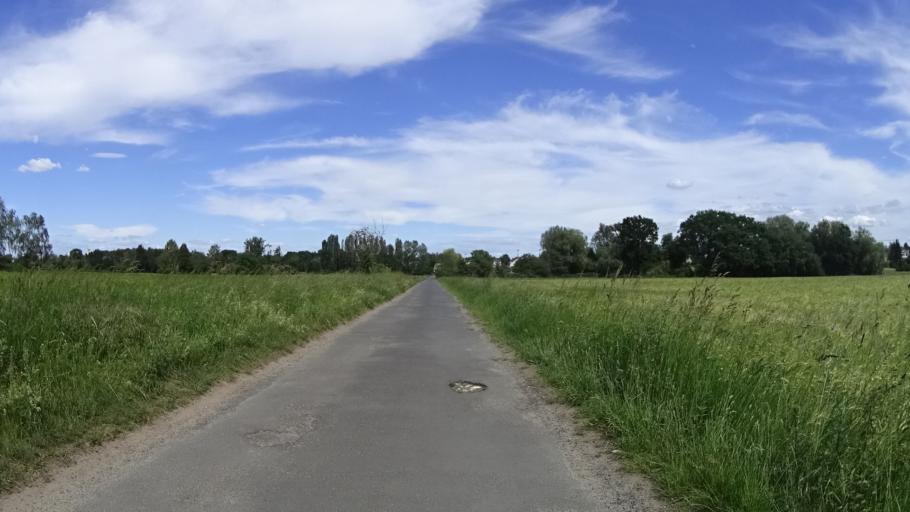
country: DE
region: Hesse
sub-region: Regierungsbezirk Darmstadt
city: Muehlheim am Main
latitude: 50.1187
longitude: 8.8018
